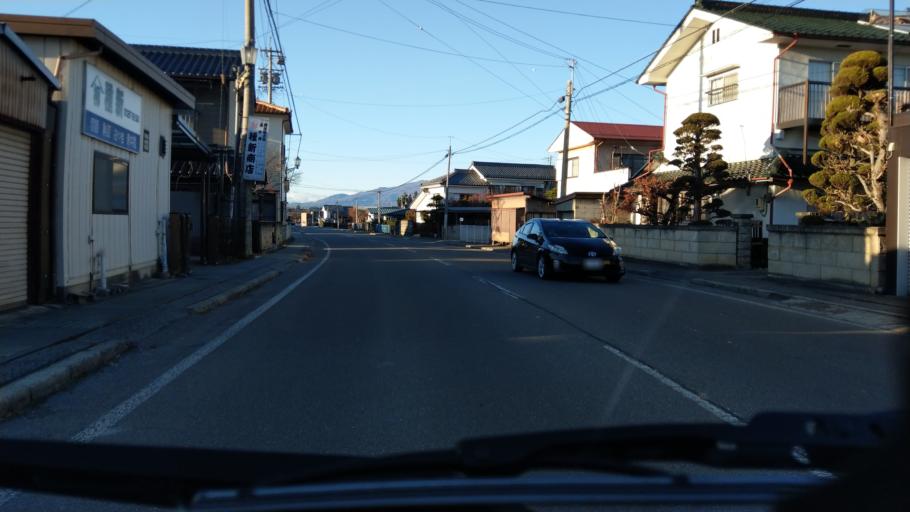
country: JP
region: Nagano
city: Saku
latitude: 36.2343
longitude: 138.4747
